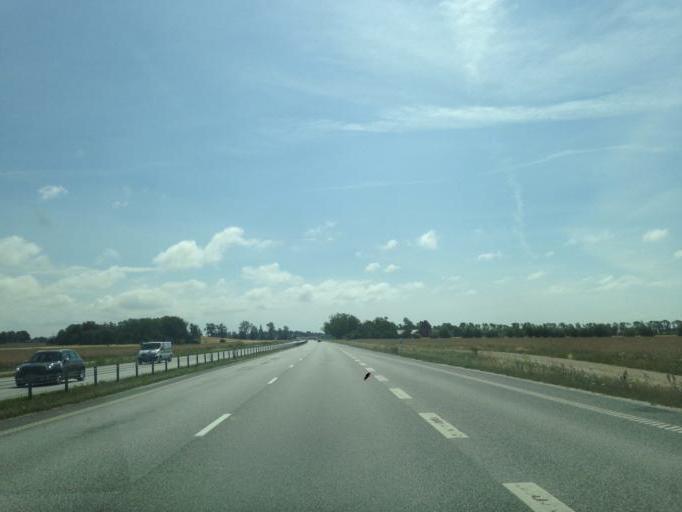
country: SE
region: Skane
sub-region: Vellinge Kommun
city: Vellinge
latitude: 55.4508
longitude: 13.0235
